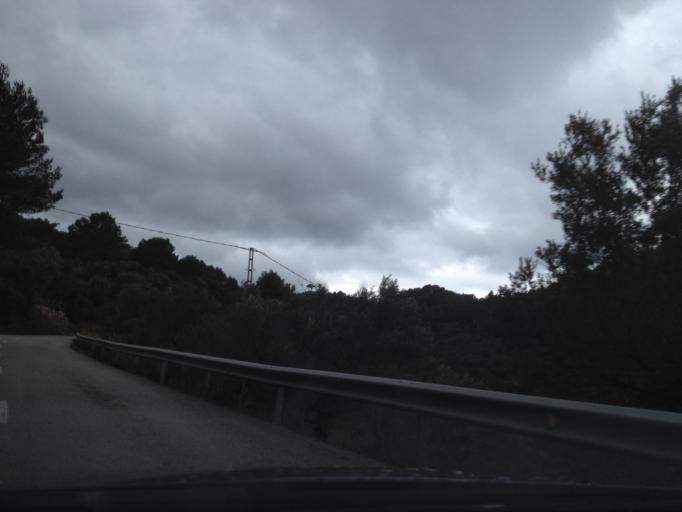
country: ES
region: Balearic Islands
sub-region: Illes Balears
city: Soller
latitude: 39.7755
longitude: 2.6864
